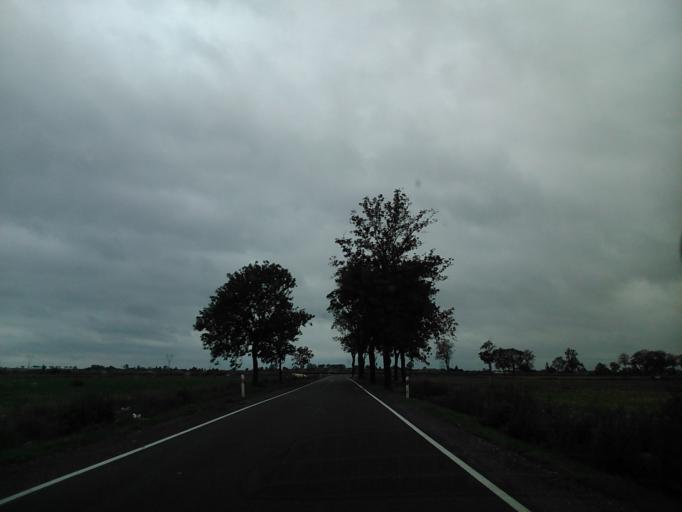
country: PL
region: Kujawsko-Pomorskie
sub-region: Powiat mogilenski
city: Strzelno
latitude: 52.6675
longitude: 18.2460
